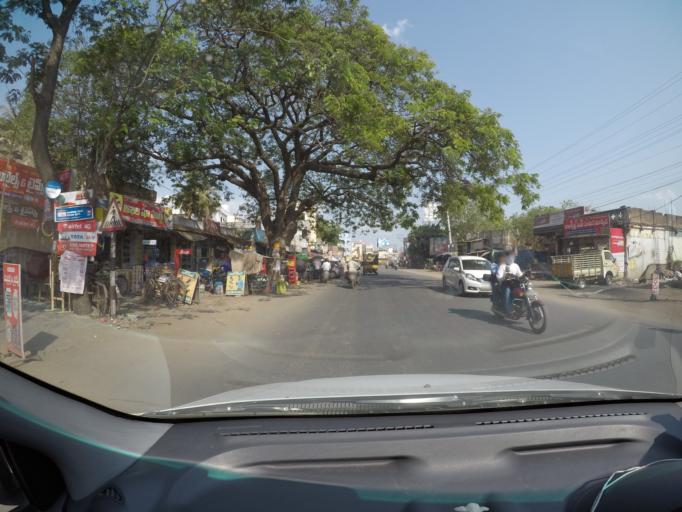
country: IN
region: Andhra Pradesh
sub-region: Krishna
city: Kankipadu
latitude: 16.4350
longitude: 80.7671
